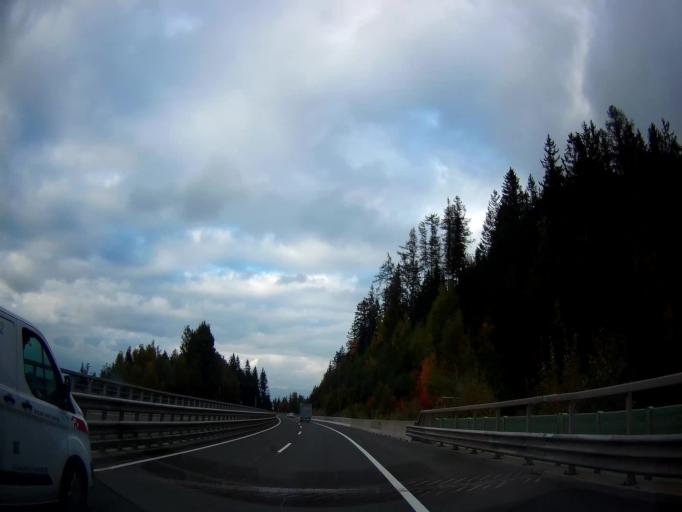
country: AT
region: Styria
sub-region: Politischer Bezirk Voitsberg
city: Voitsberg
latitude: 46.9846
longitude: 15.1217
